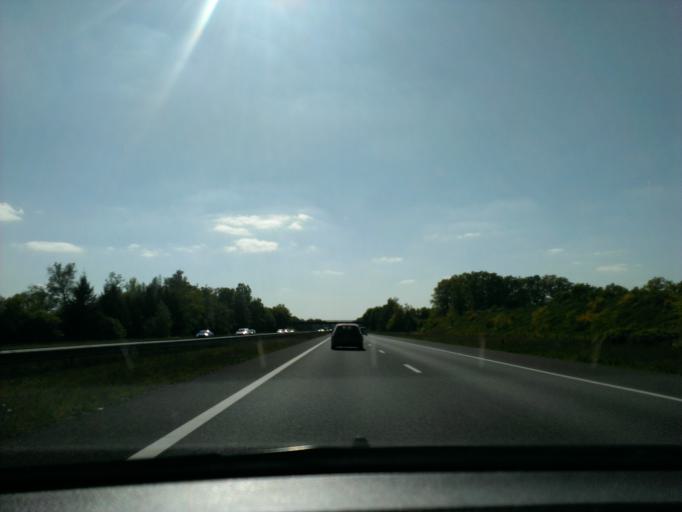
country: NL
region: Overijssel
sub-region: Gemeente Hof van Twente
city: Goor
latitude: 52.2884
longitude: 6.6153
